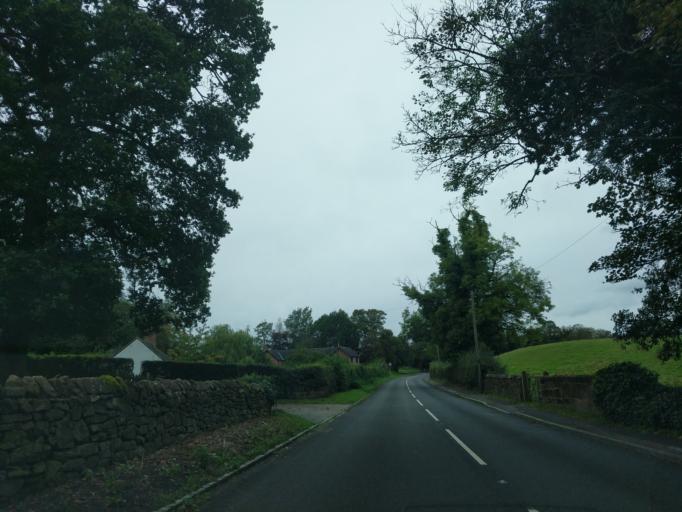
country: GB
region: England
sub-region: Cheshire East
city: Chorlton
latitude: 53.0387
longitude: -2.3711
